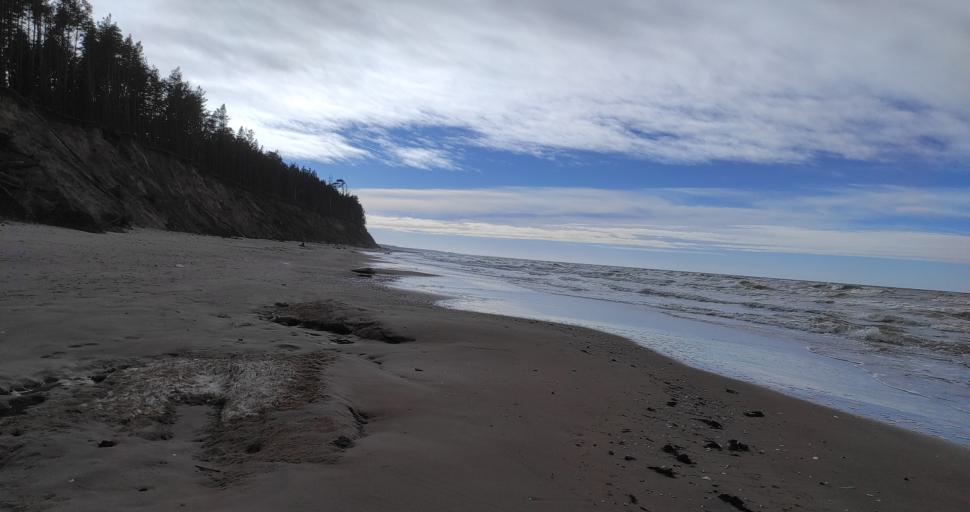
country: LV
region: Alsunga
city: Alsunga
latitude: 57.0231
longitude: 21.3907
